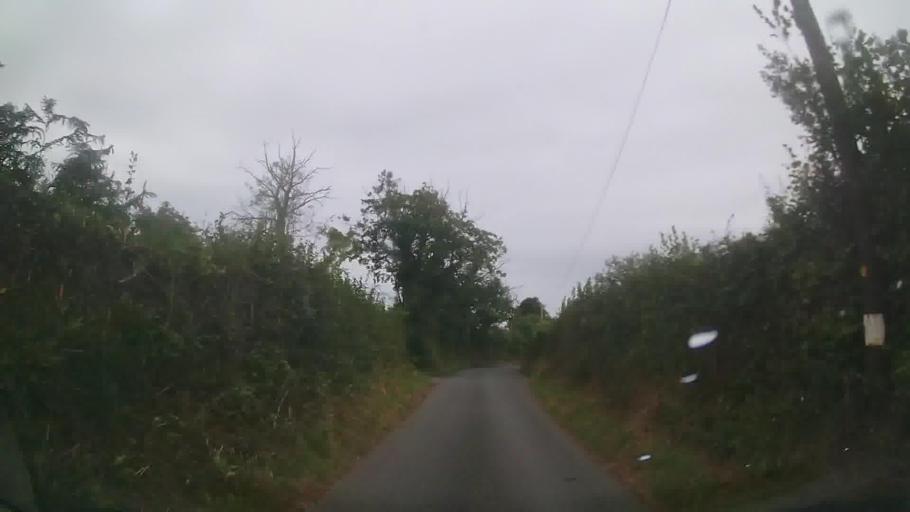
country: GB
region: Wales
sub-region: Pembrokeshire
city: Saundersfoot
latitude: 51.7434
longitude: -4.6599
